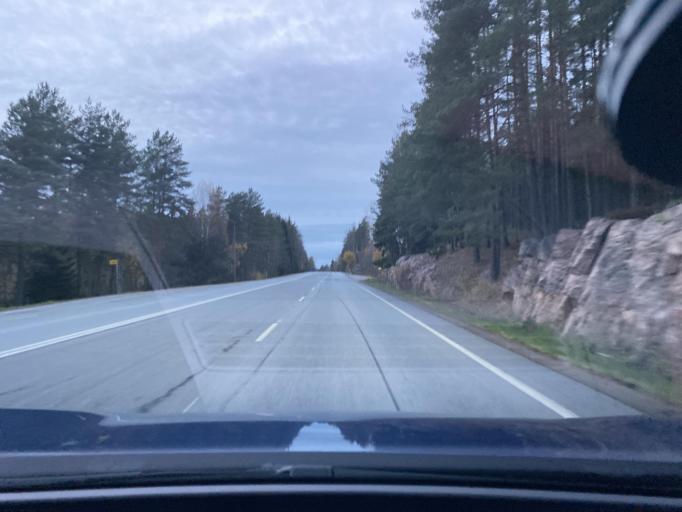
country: FI
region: Uusimaa
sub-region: Helsinki
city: Sammatti
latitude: 60.3857
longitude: 23.8642
